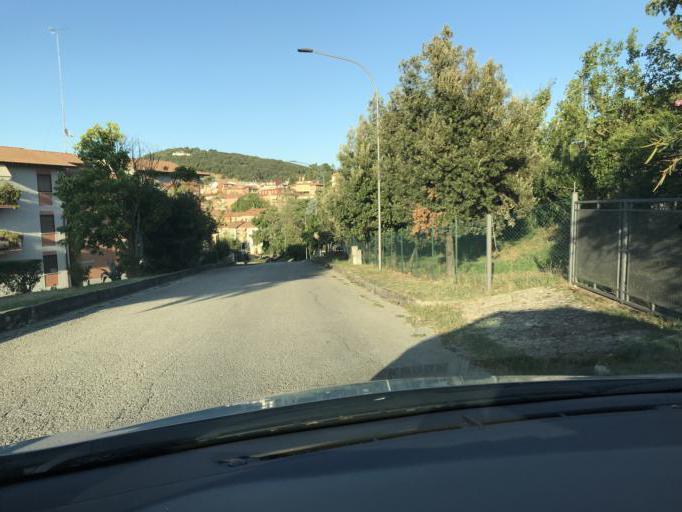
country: IT
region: Umbria
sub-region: Provincia di Terni
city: Amelia
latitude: 42.5466
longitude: 12.4147
